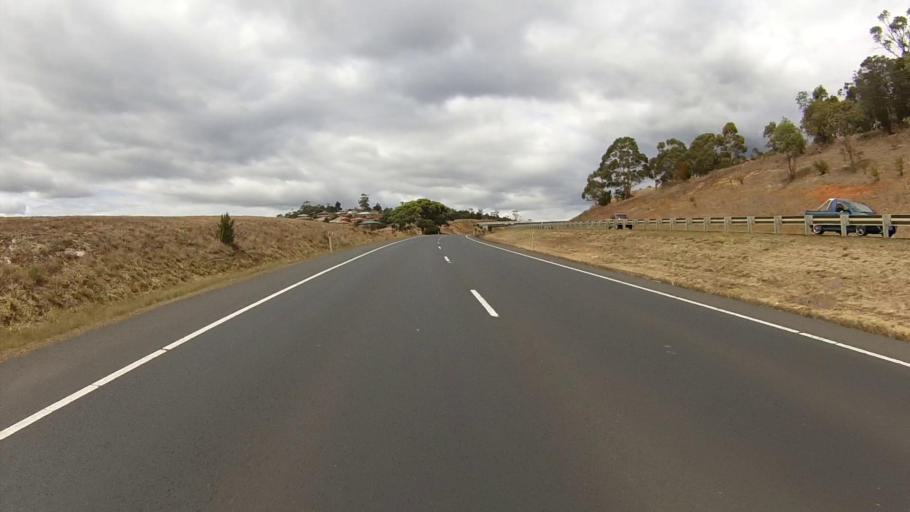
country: AU
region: Tasmania
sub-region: Glenorchy
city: Austins Ferry
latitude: -42.7708
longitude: 147.2381
